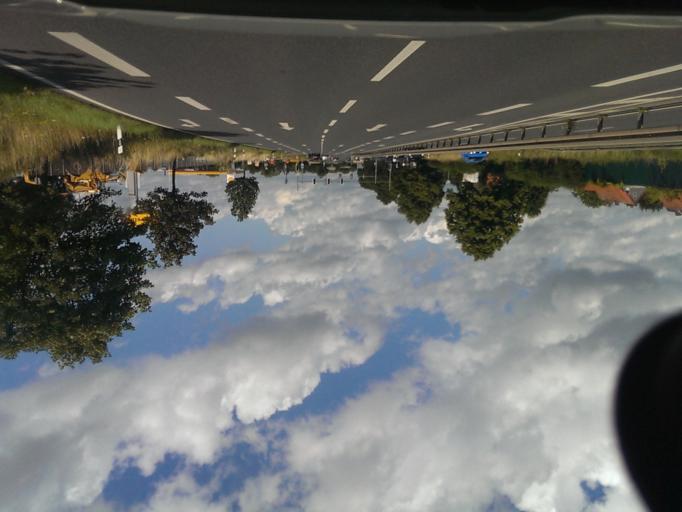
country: DE
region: Lower Saxony
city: Sarstedt
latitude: 52.2728
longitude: 9.8483
